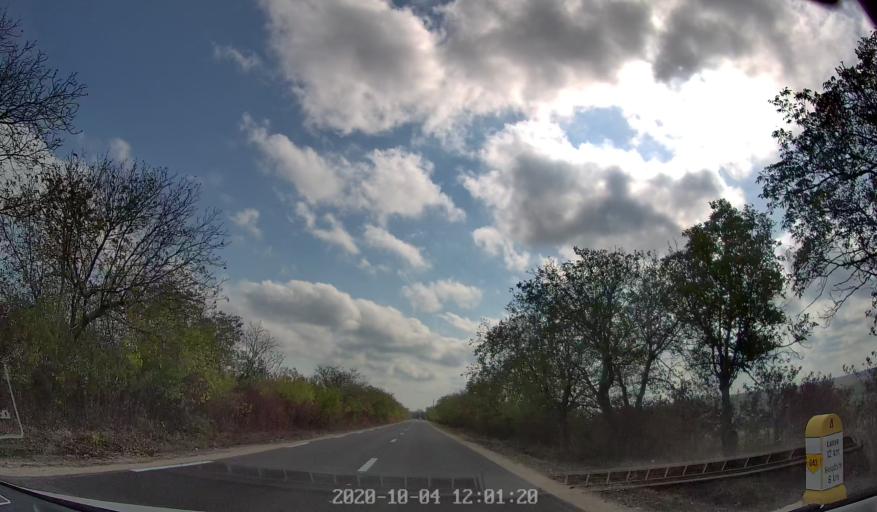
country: MD
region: Rezina
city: Saharna
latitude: 47.6258
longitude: 28.8873
